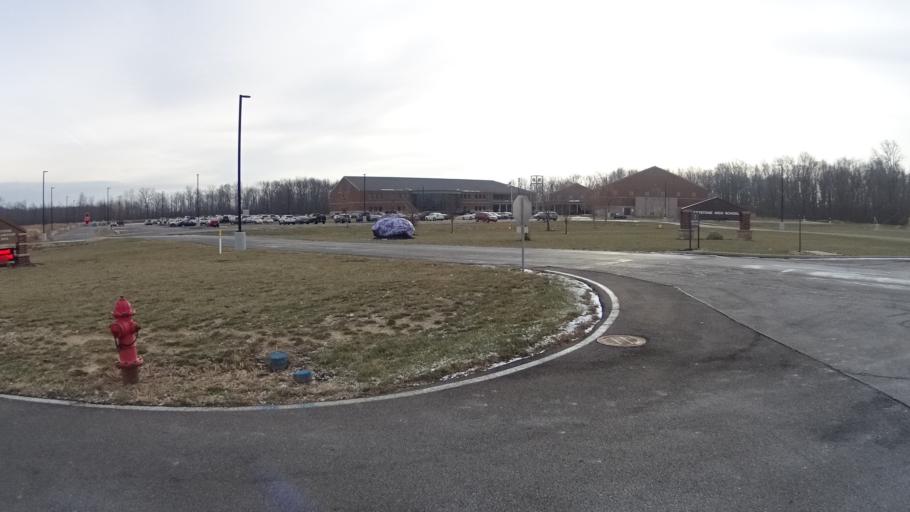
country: US
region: Ohio
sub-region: Lorain County
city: Lagrange
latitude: 41.2322
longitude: -82.1075
